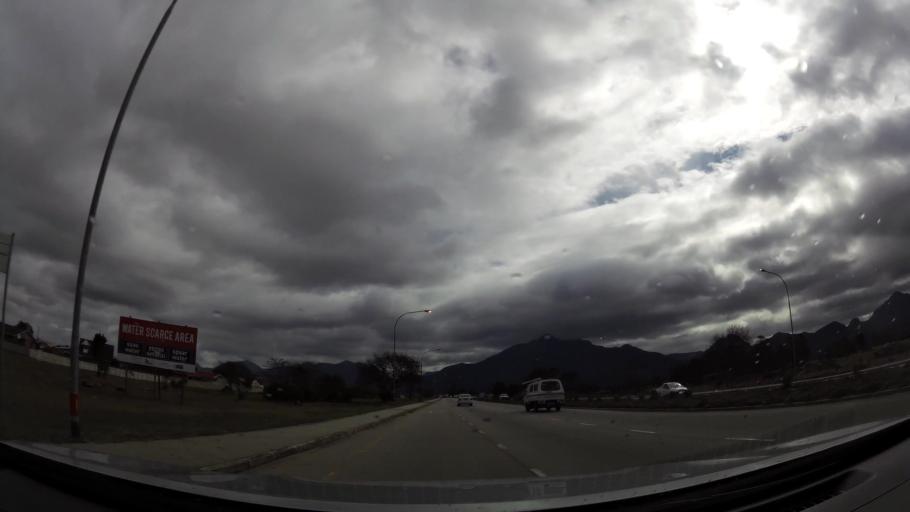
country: ZA
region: Western Cape
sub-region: Eden District Municipality
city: George
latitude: -33.9768
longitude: 22.4943
